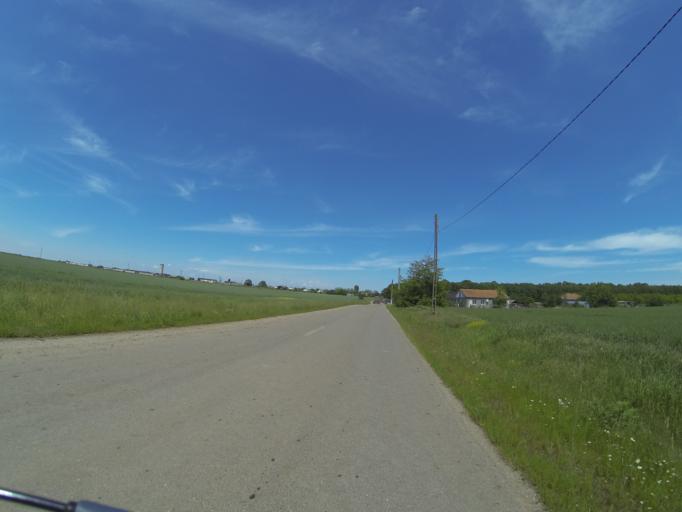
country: RO
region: Dolj
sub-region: Comuna Teslui
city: Teslui
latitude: 44.1664
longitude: 24.1605
